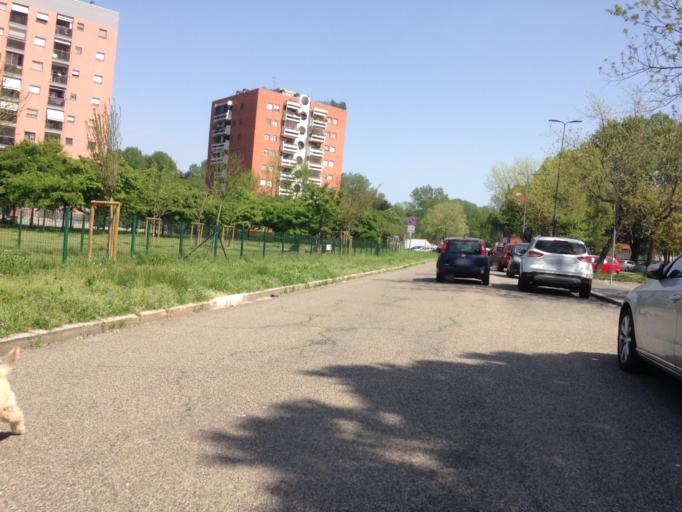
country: IT
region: Lombardy
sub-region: Citta metropolitana di Milano
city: Milano
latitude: 45.4252
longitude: 9.1781
